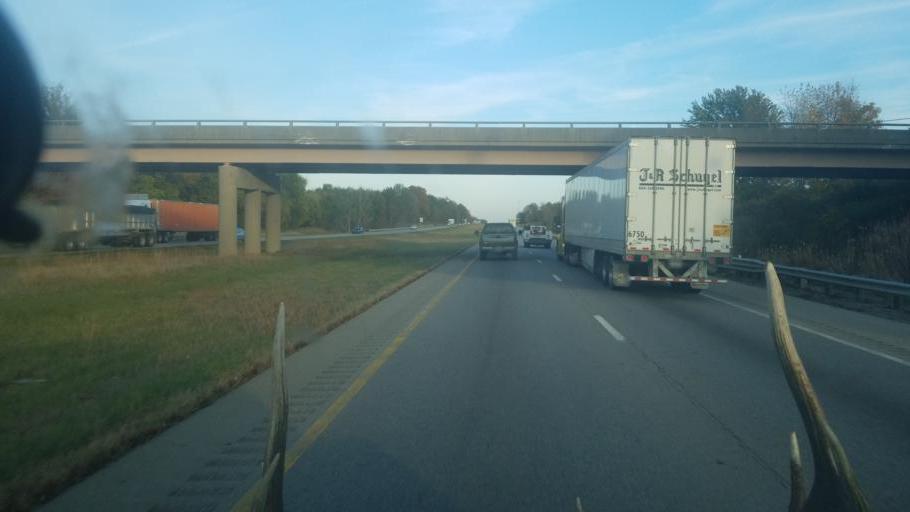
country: US
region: Ohio
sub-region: Licking County
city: Etna
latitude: 39.9469
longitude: -82.6485
